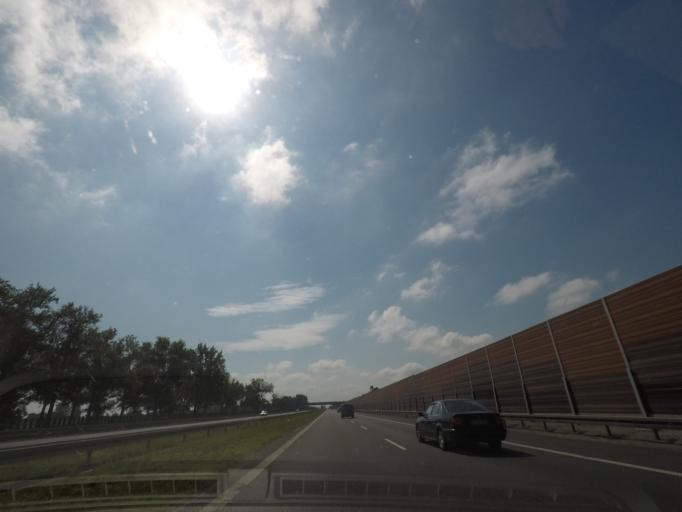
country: PL
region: Kujawsko-Pomorskie
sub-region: Powiat aleksandrowski
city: Raciazek
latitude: 52.8120
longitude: 18.8121
